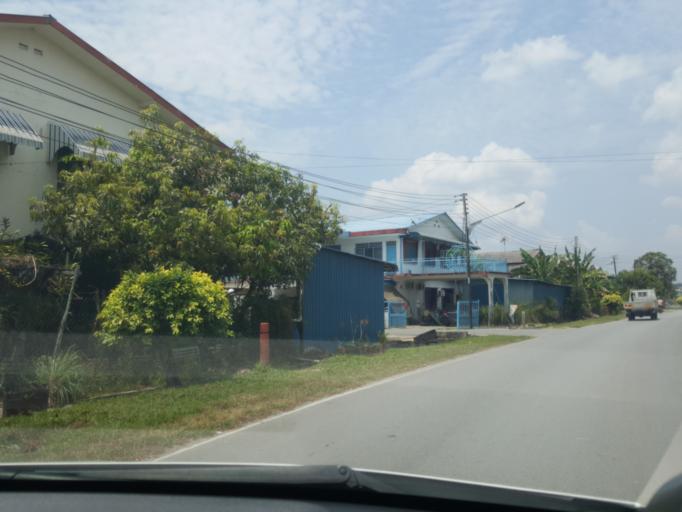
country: MY
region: Sarawak
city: Sarikei
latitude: 2.1261
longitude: 111.5240
